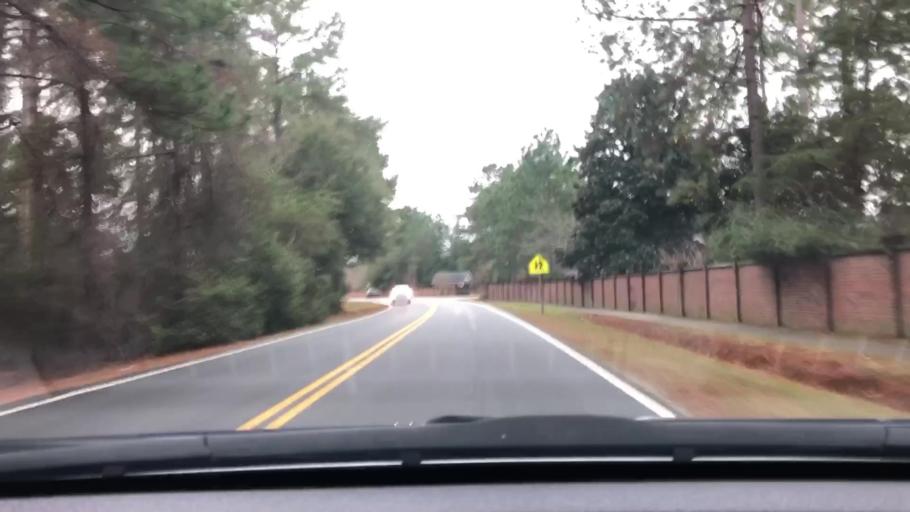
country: US
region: South Carolina
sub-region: Sumter County
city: Cherryvale
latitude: 33.9395
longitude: -80.4047
